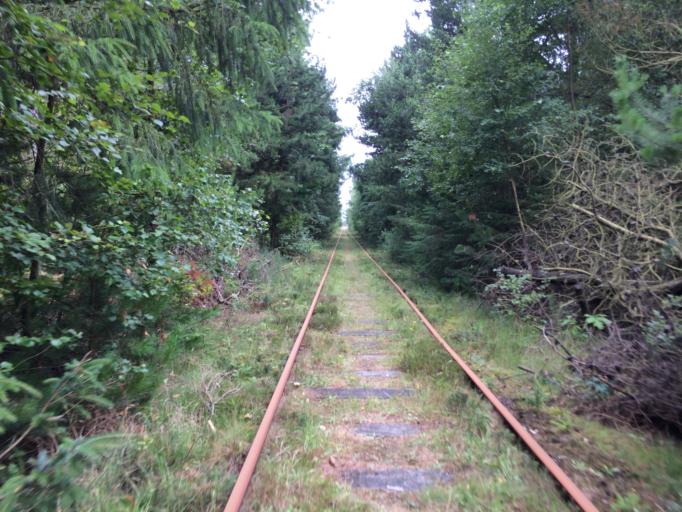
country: DK
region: South Denmark
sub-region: Varde Kommune
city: Oksbol
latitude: 55.7985
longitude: 8.2233
